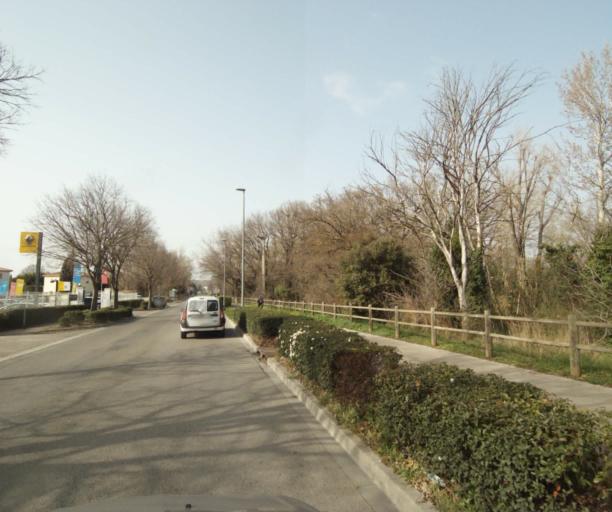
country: FR
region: Provence-Alpes-Cote d'Azur
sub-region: Departement des Bouches-du-Rhone
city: Les Pennes-Mirabeau
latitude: 43.4191
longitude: 5.2911
